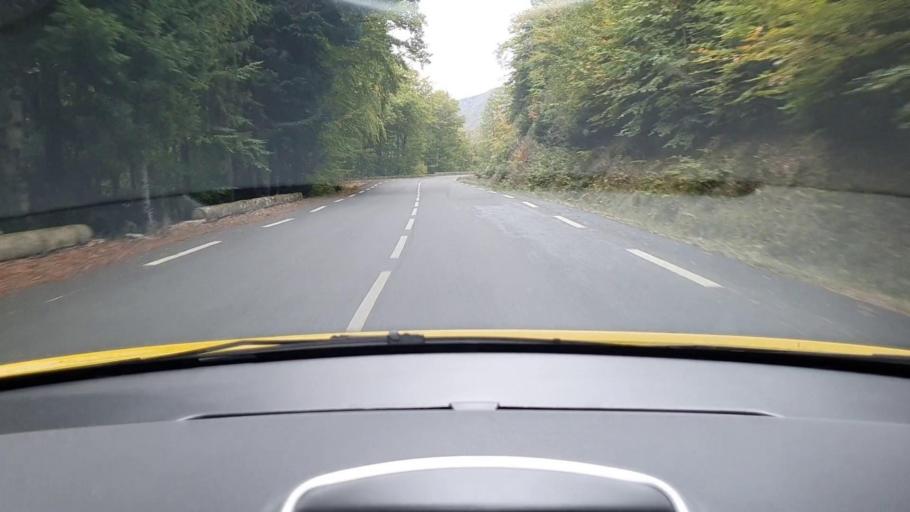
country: FR
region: Languedoc-Roussillon
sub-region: Departement du Gard
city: Valleraugue
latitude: 44.0955
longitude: 3.5553
